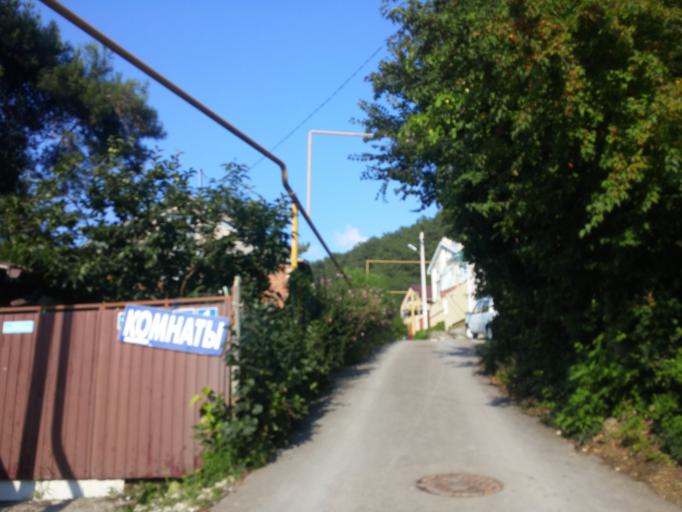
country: RU
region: Krasnodarskiy
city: Divnomorskoye
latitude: 44.4648
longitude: 38.1596
